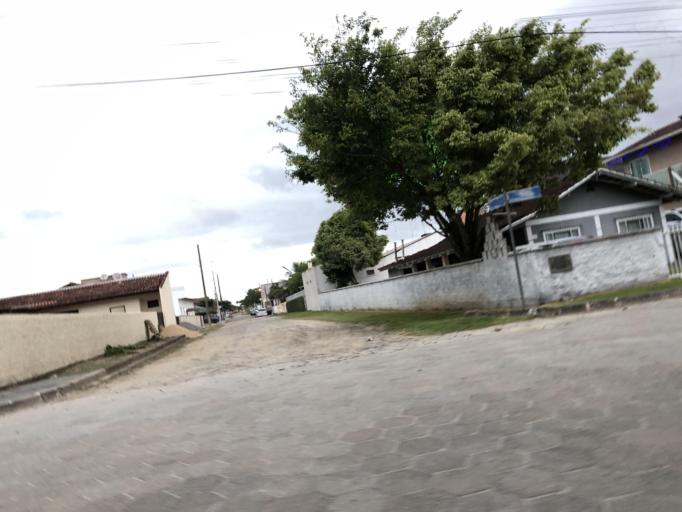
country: BR
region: Santa Catarina
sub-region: Sao Francisco Do Sul
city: Sao Francisco do Sul
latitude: -26.2146
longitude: -48.5261
